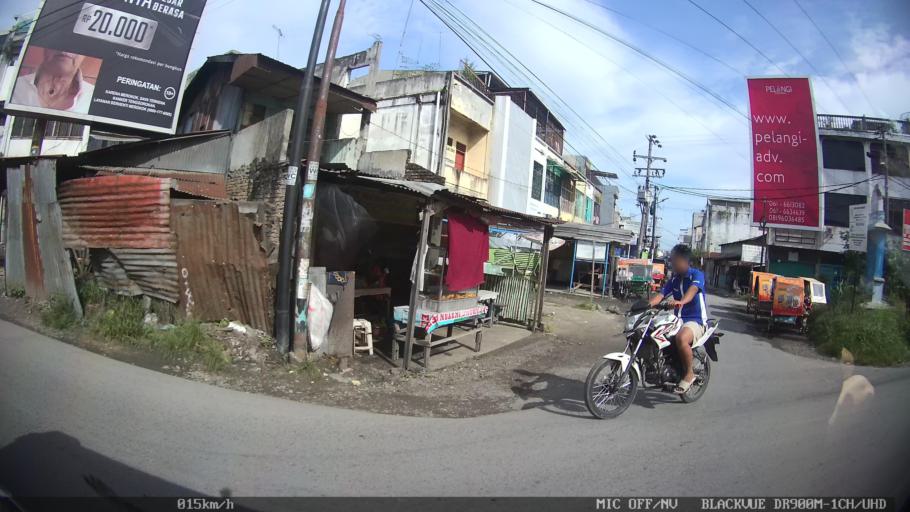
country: ID
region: North Sumatra
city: Medan
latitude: 3.6267
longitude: 98.6604
